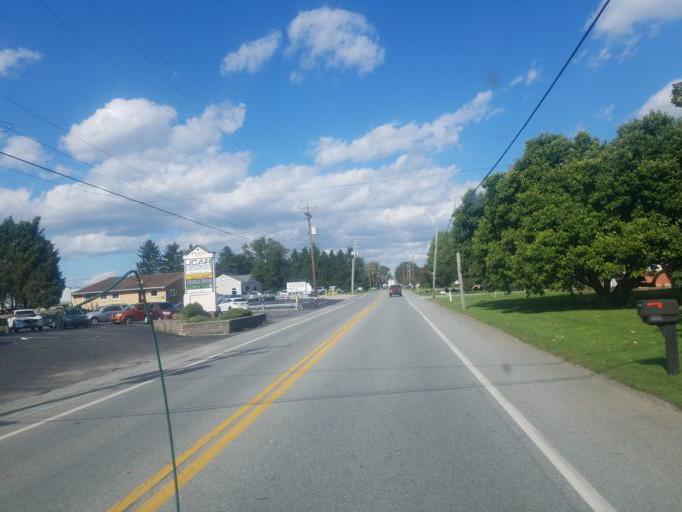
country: US
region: Pennsylvania
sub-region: York County
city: North York
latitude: 39.9997
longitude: -76.7340
